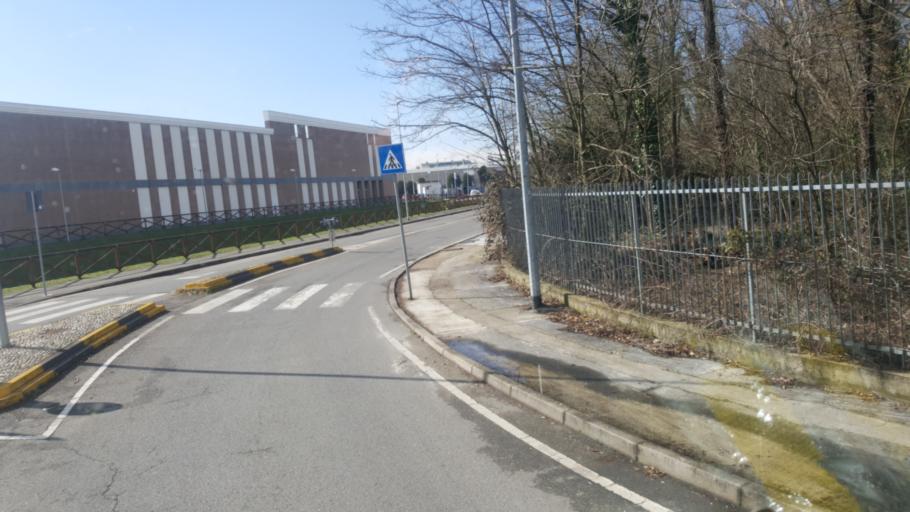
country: IT
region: Lombardy
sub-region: Citta metropolitana di Milano
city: Rozzano
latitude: 45.3782
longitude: 9.1715
